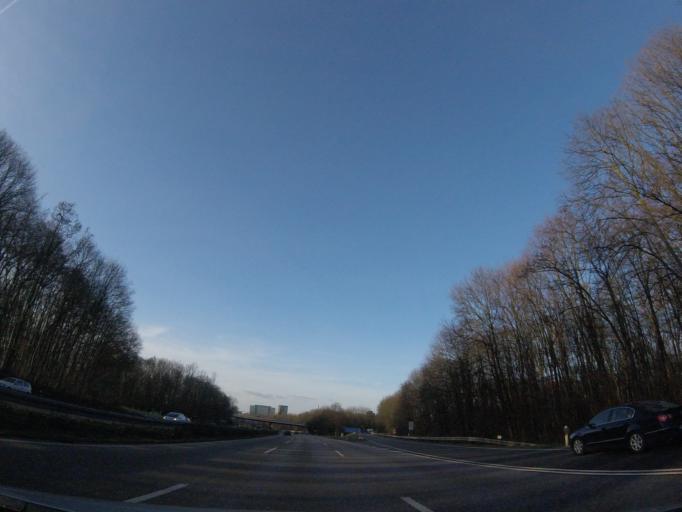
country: DE
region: Hesse
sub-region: Regierungsbezirk Darmstadt
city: Offenbach
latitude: 50.0935
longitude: 8.7404
